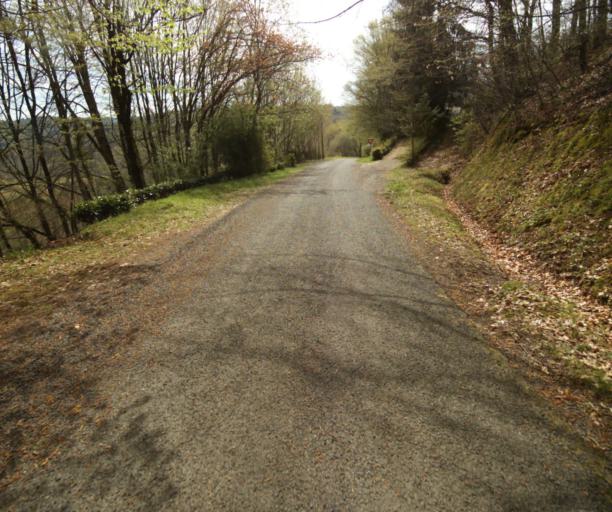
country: FR
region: Limousin
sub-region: Departement de la Correze
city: Laguenne
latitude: 45.2548
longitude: 1.8182
